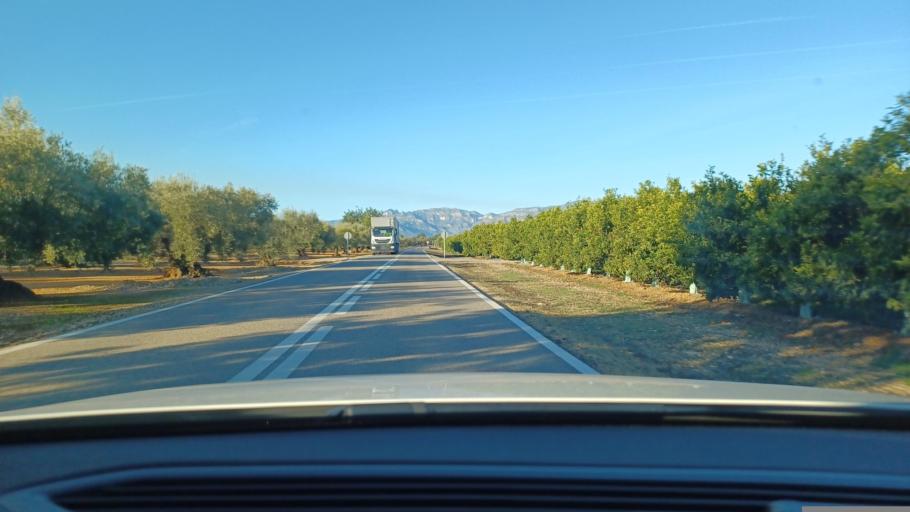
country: ES
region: Catalonia
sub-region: Provincia de Tarragona
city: Santa Barbara
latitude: 40.7198
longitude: 0.4610
